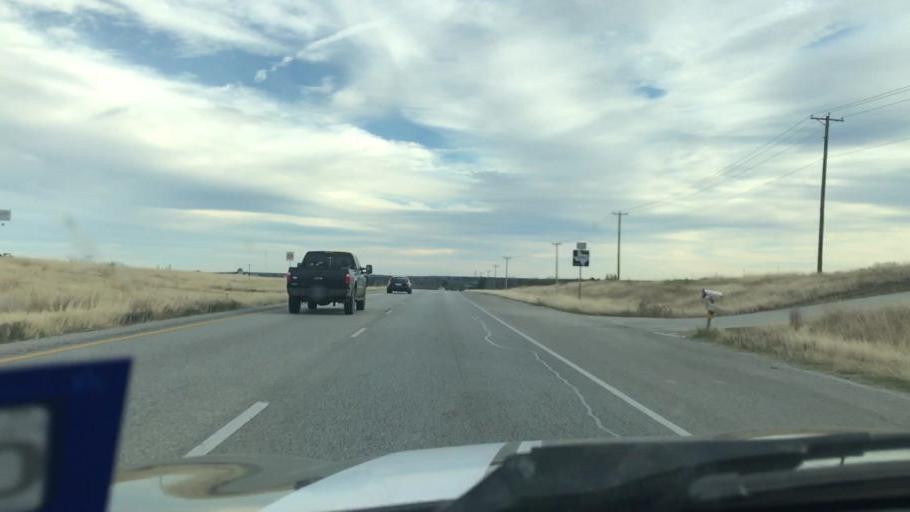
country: US
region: Texas
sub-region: Bastrop County
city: Elgin
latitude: 30.3135
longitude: -97.3088
